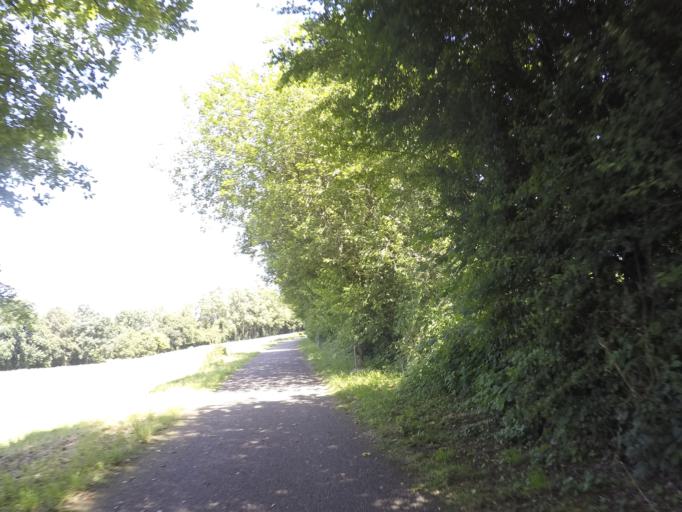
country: BE
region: Wallonia
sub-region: Province de Namur
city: Ciney
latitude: 50.3175
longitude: 5.1067
